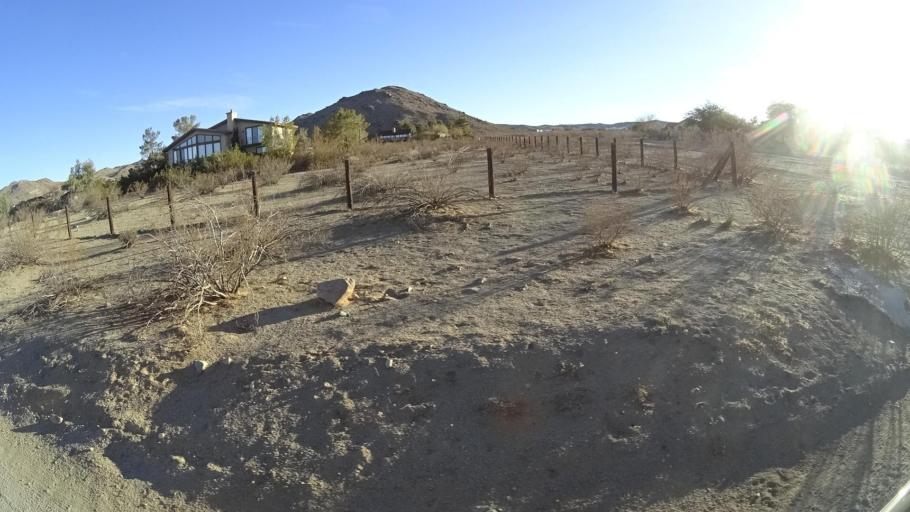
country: US
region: California
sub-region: Kern County
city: Ridgecrest
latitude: 35.5824
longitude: -117.6610
